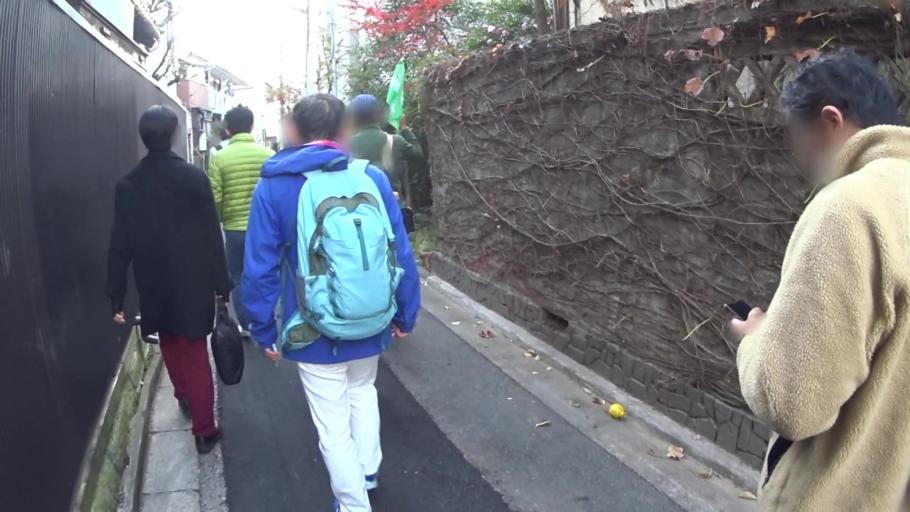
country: JP
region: Tokyo
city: Urayasu
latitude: 35.7191
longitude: 139.8125
